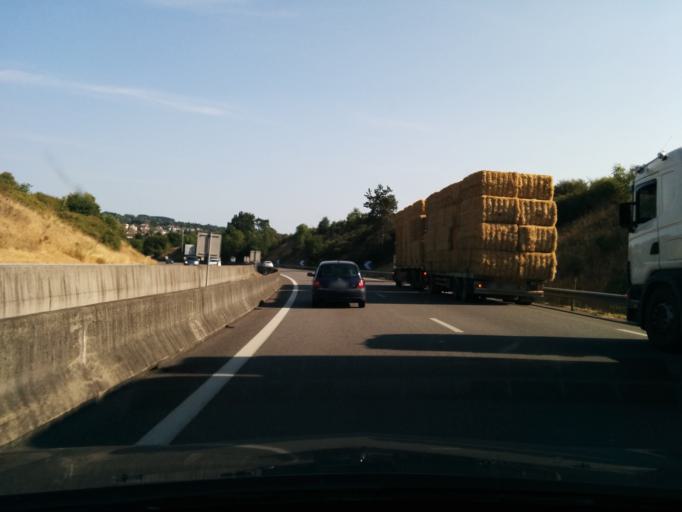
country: FR
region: Limousin
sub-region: Departement de la Haute-Vienne
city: Pierre-Buffiere
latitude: 45.7028
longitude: 1.3540
